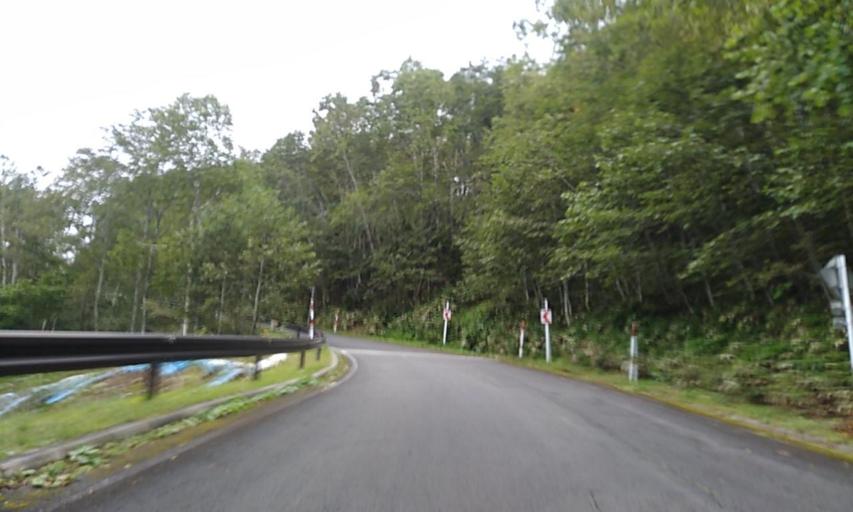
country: JP
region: Hokkaido
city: Bihoro
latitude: 43.5783
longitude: 144.2364
